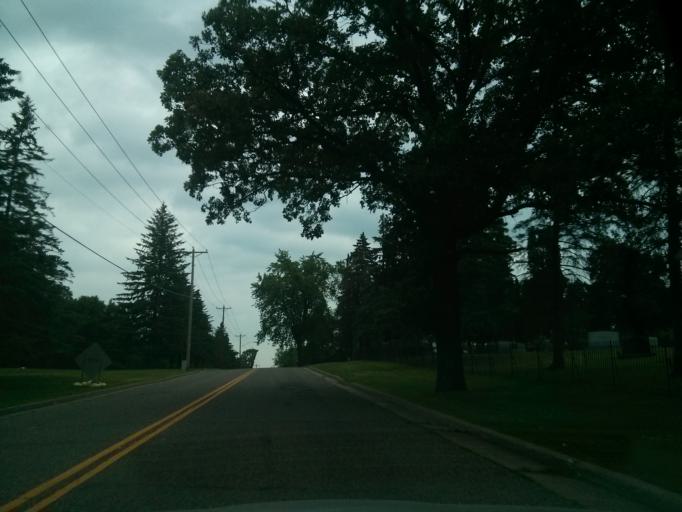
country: US
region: Wisconsin
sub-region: Saint Croix County
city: Hudson
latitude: 44.9732
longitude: -92.7463
